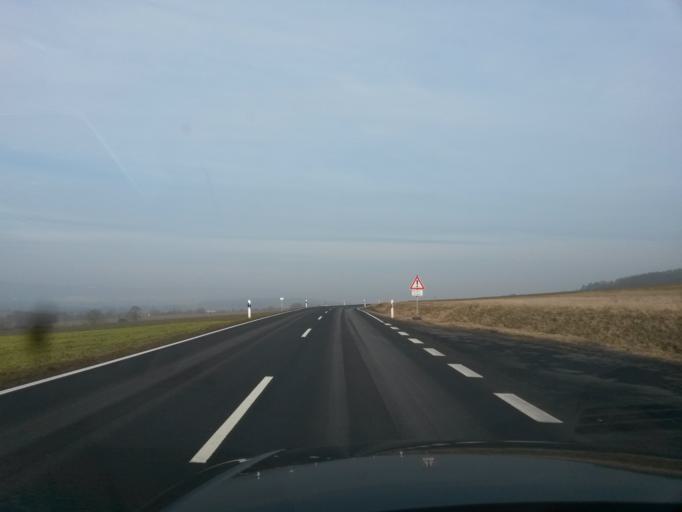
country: DE
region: Bavaria
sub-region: Regierungsbezirk Unterfranken
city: Ostheim vor der Rhon
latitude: 50.4691
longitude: 10.2032
